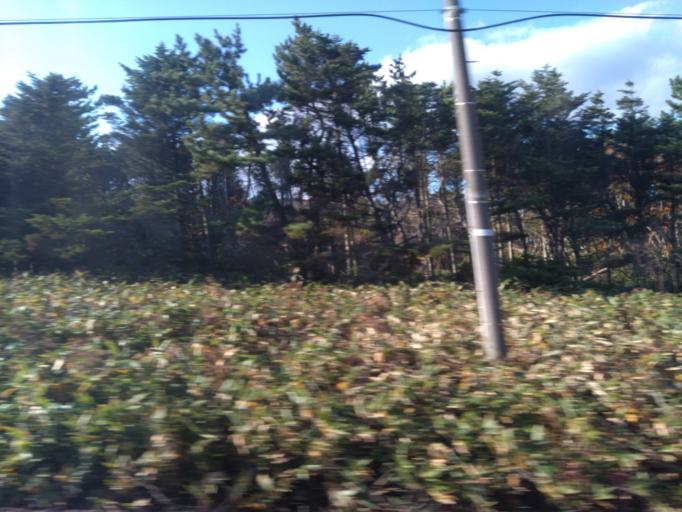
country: JP
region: Hokkaido
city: Niseko Town
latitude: 42.5731
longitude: 140.4454
